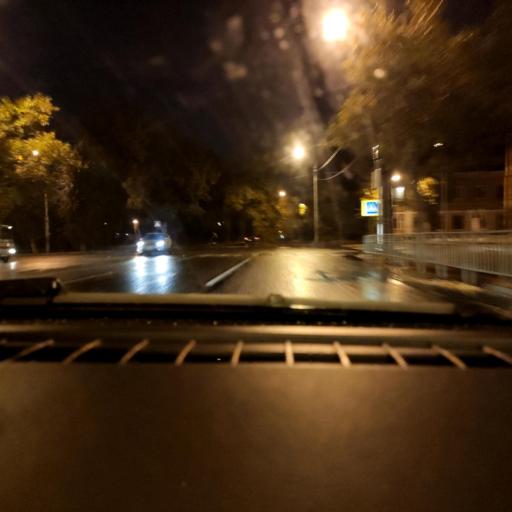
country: RU
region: Voronezj
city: Maslovka
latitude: 51.6188
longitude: 39.2503
